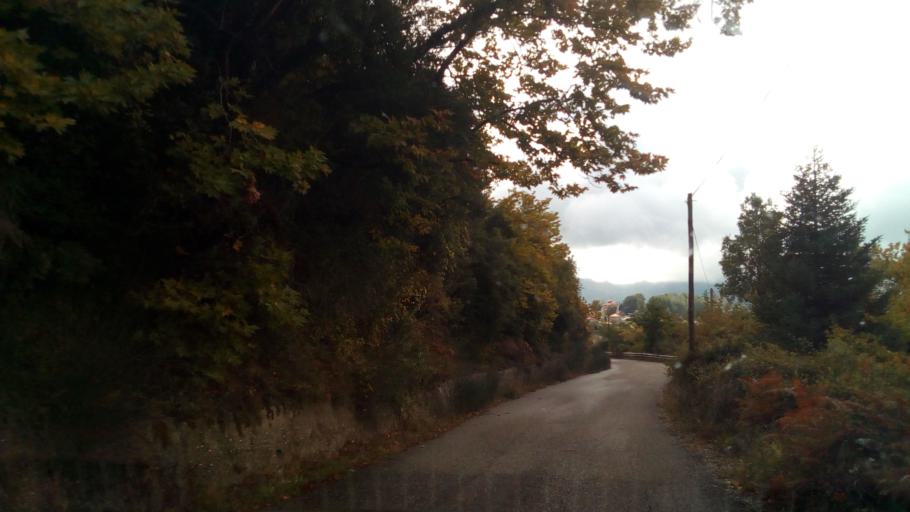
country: GR
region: West Greece
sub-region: Nomos Aitolias kai Akarnanias
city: Nafpaktos
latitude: 38.5404
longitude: 21.8164
